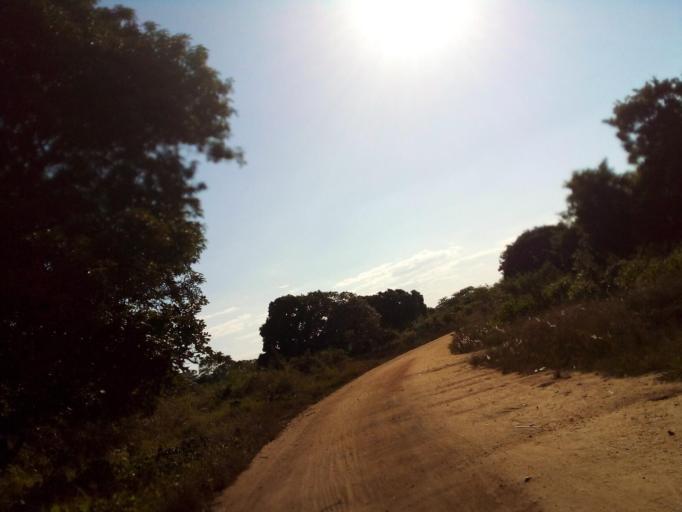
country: MZ
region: Zambezia
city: Quelimane
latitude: -17.5042
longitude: 36.5831
